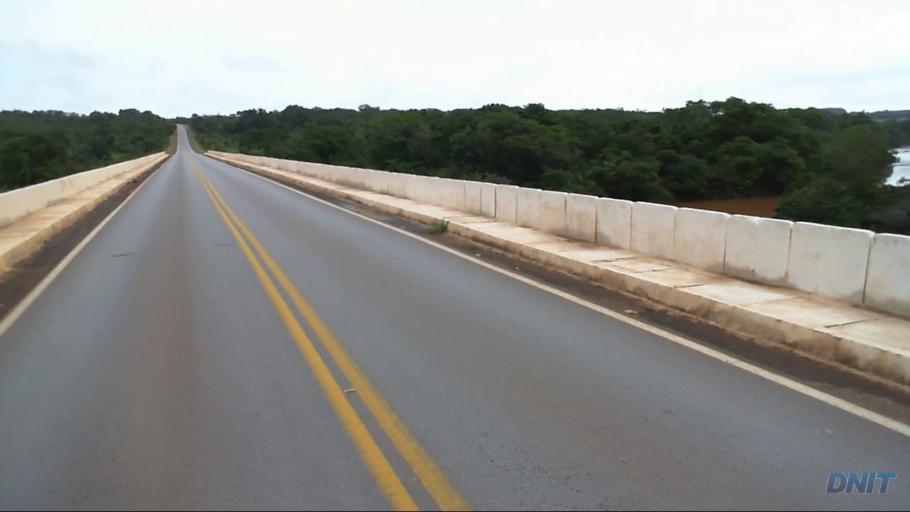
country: BR
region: Goias
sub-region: Uruacu
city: Uruacu
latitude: -14.7488
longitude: -49.0751
